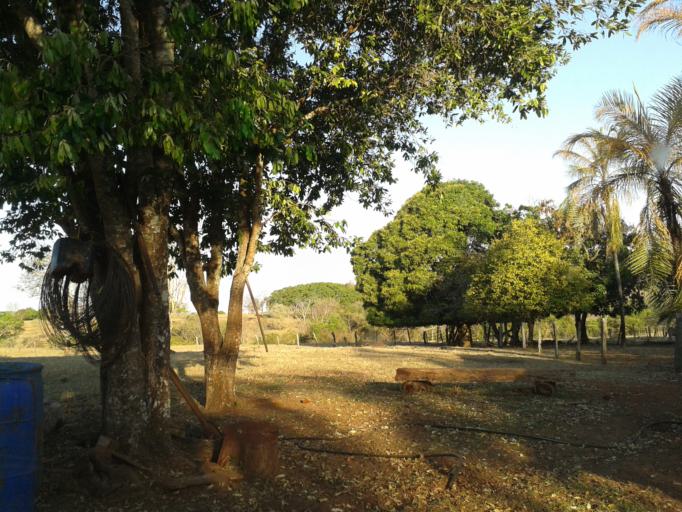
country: BR
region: Minas Gerais
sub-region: Campina Verde
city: Campina Verde
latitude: -19.2671
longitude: -49.6058
